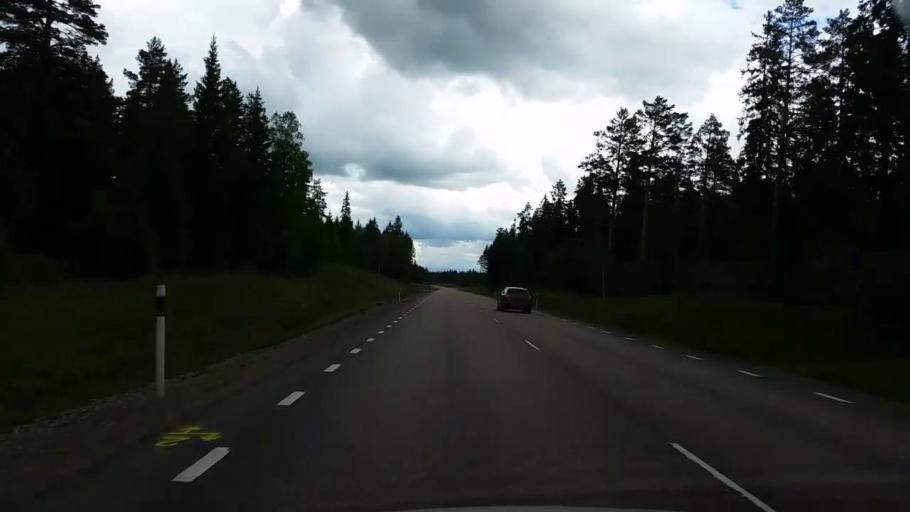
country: SE
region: Dalarna
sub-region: Avesta Kommun
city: Horndal
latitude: 60.4601
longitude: 16.4463
